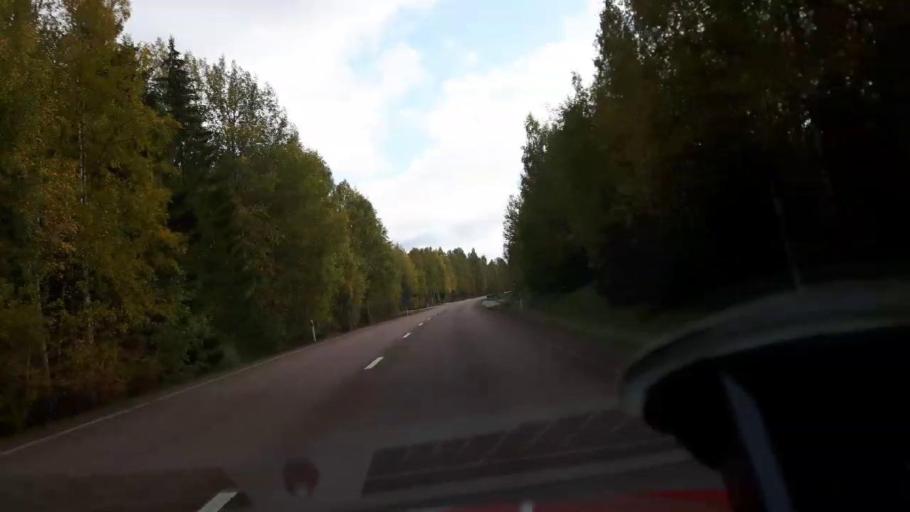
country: SE
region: Gaevleborg
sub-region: Ljusdals Kommun
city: Jaervsoe
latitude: 61.6444
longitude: 16.2171
